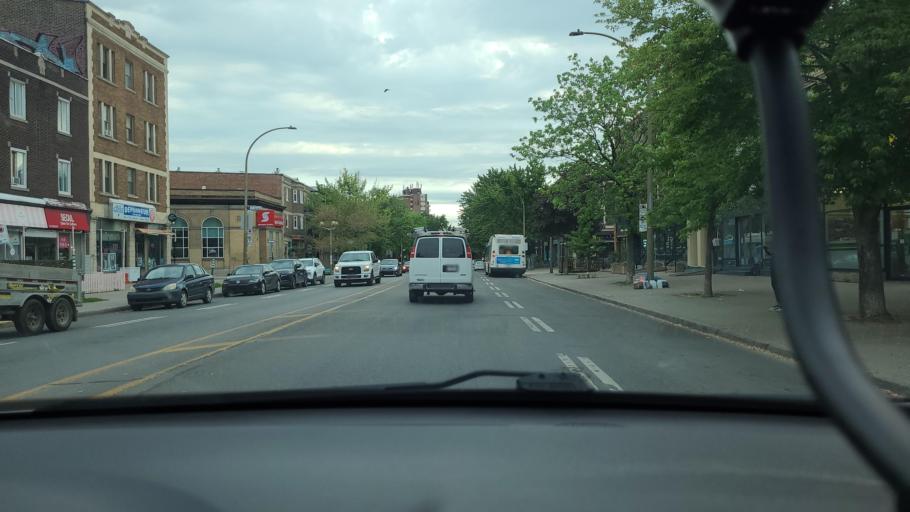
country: CA
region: Quebec
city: Saint-Raymond
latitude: 45.4704
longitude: -73.6161
